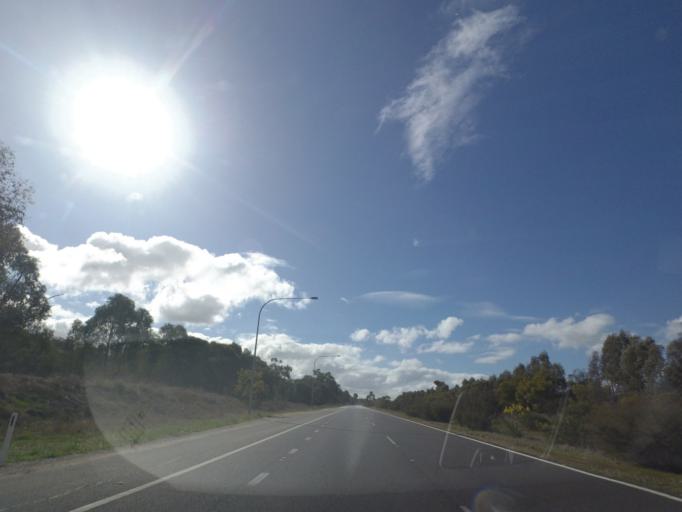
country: AU
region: New South Wales
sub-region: Albury Municipality
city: Lavington
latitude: -36.0341
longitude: 146.9757
